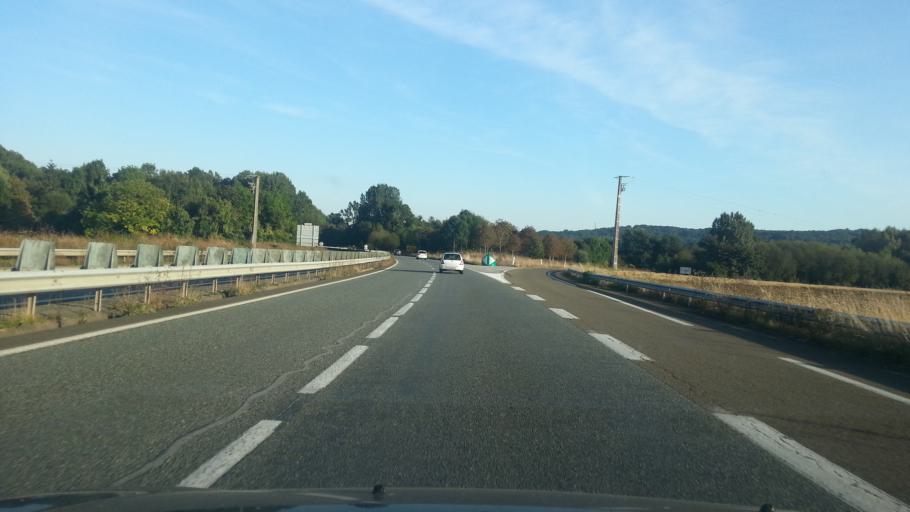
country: FR
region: Picardie
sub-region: Departement de l'Oise
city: Agnetz
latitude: 49.3923
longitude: 2.3817
